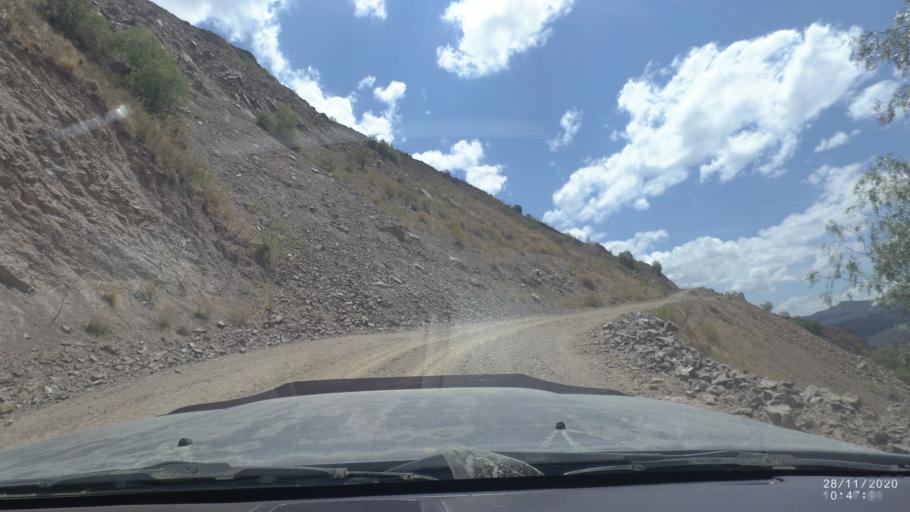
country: BO
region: Cochabamba
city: Capinota
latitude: -17.7859
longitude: -66.1244
